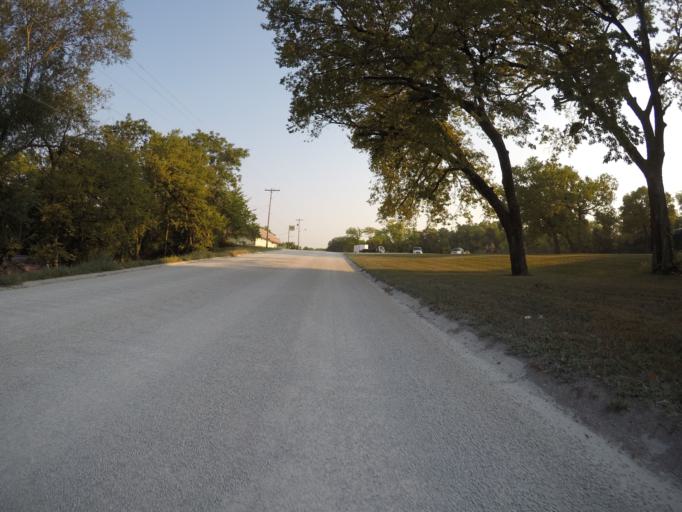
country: US
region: Kansas
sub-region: Marshall County
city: Marysville
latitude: 39.8473
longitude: -96.6481
